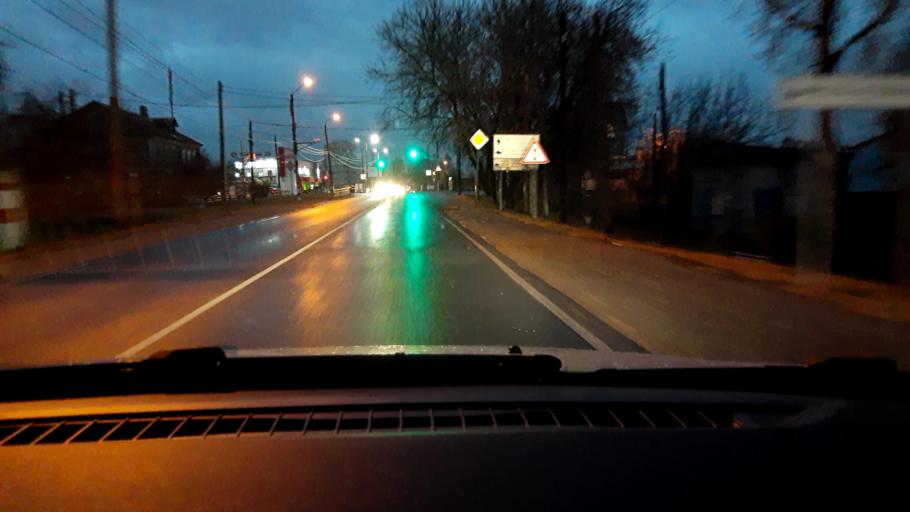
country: RU
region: Nizjnij Novgorod
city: Bor
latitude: 56.3763
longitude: 44.0281
